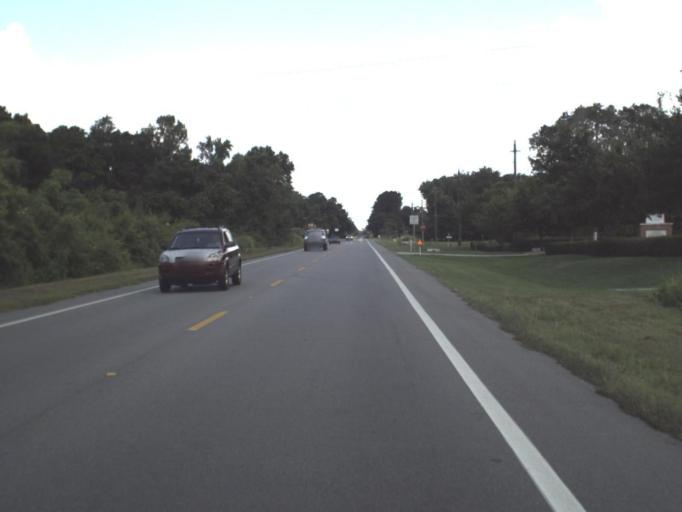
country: US
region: Florida
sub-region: Putnam County
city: Crescent City
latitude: 29.4532
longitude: -81.5151
